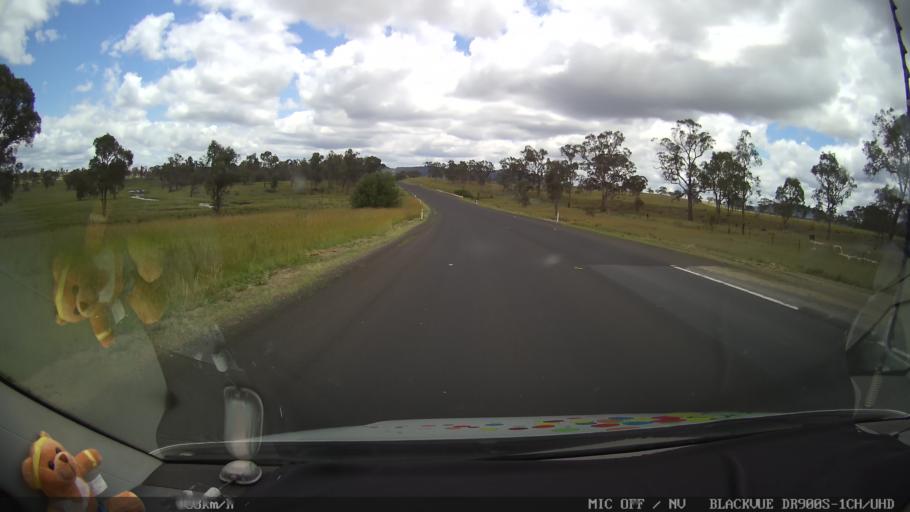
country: AU
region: New South Wales
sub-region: Glen Innes Severn
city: Glen Innes
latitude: -29.3882
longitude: 151.8885
